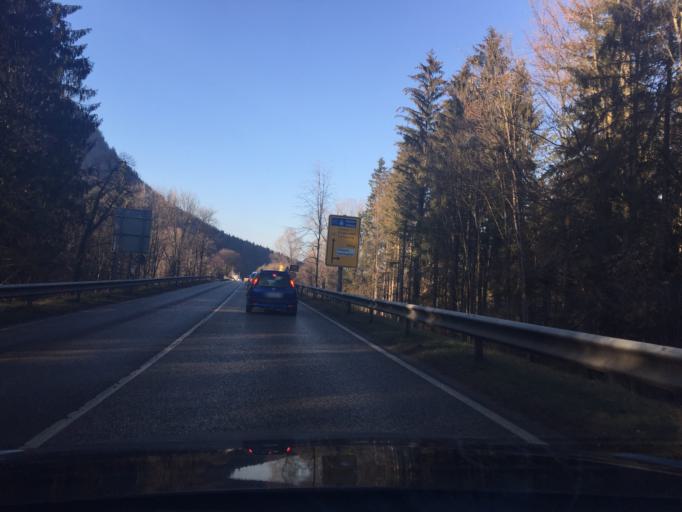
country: DE
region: Bavaria
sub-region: Upper Bavaria
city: Piding
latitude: 47.7491
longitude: 12.9061
